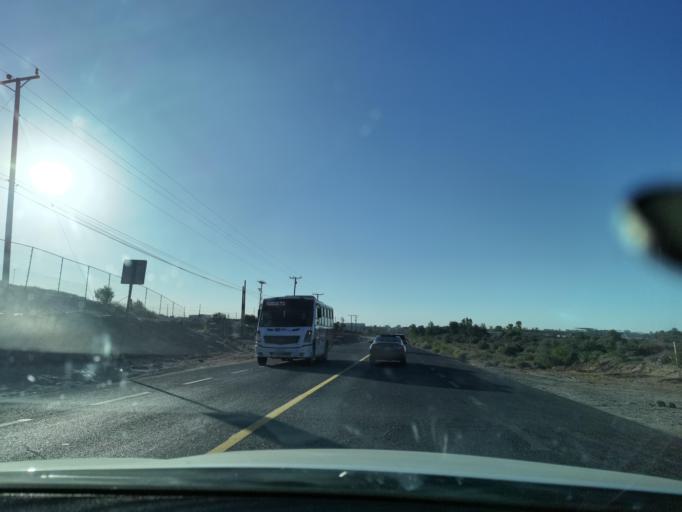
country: MX
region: Baja California
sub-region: Mexicali
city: Islas Agrarias Grupo A
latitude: 32.6393
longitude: -115.2965
